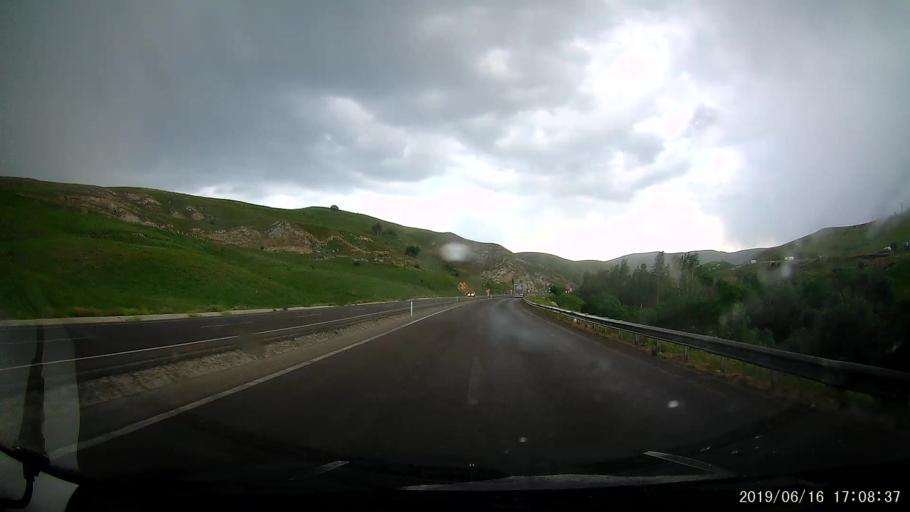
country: TR
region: Erzurum
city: Askale
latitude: 39.9061
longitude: 40.6595
